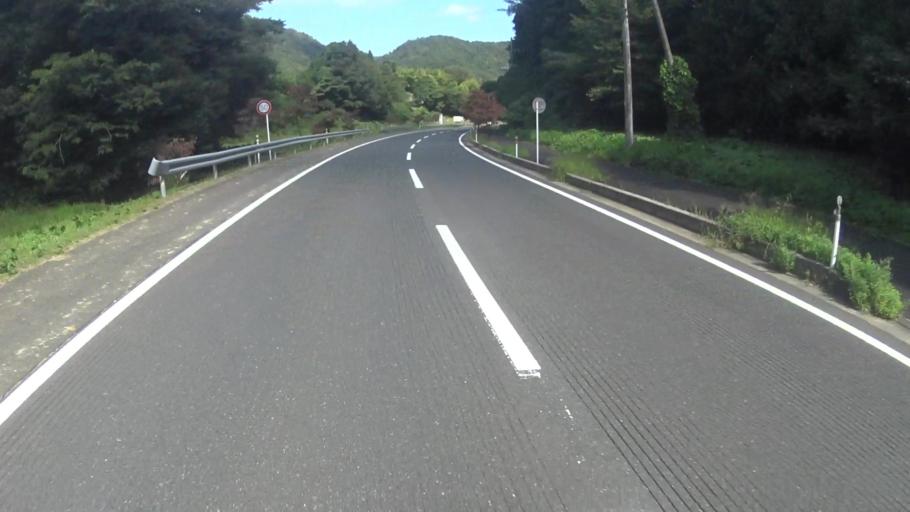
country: JP
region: Kyoto
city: Miyazu
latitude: 35.6658
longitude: 135.2619
